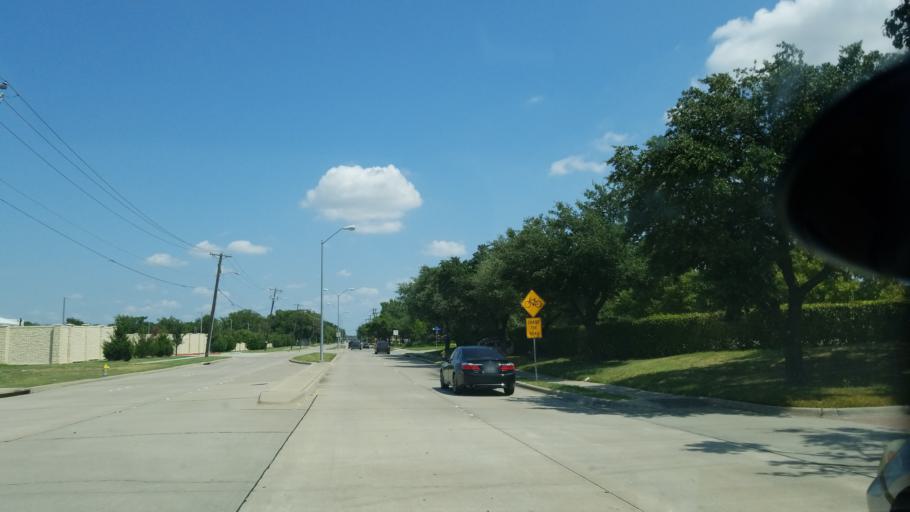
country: US
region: Texas
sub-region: Dallas County
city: Richardson
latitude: 32.9264
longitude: -96.7358
